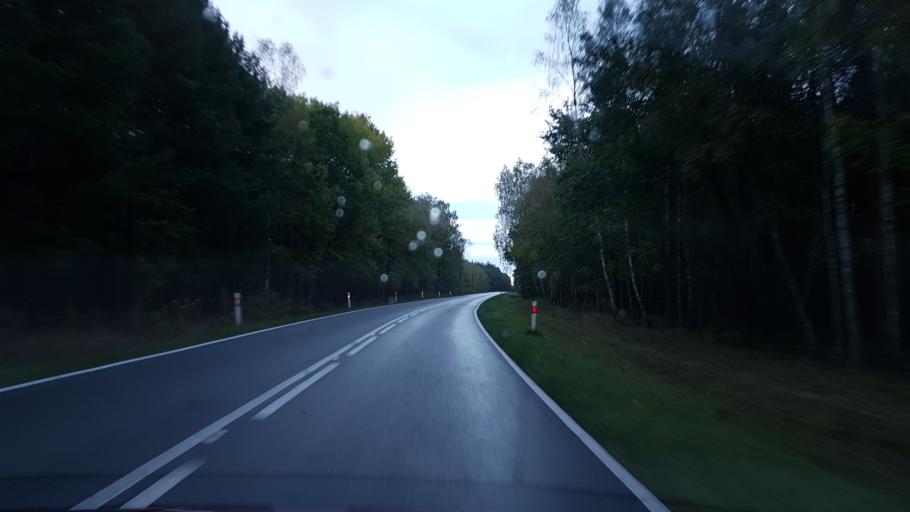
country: PL
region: Greater Poland Voivodeship
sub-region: Powiat zlotowski
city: Krajenka
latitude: 53.2791
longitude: 16.9565
